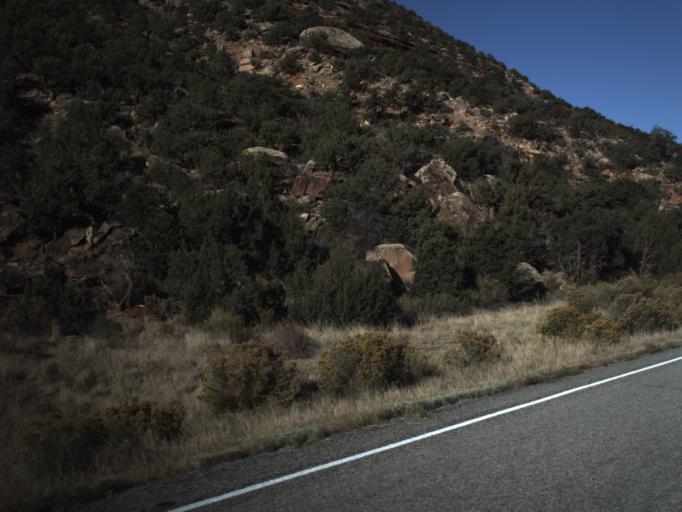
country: US
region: Utah
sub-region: San Juan County
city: Blanding
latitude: 37.5947
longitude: -110.0452
